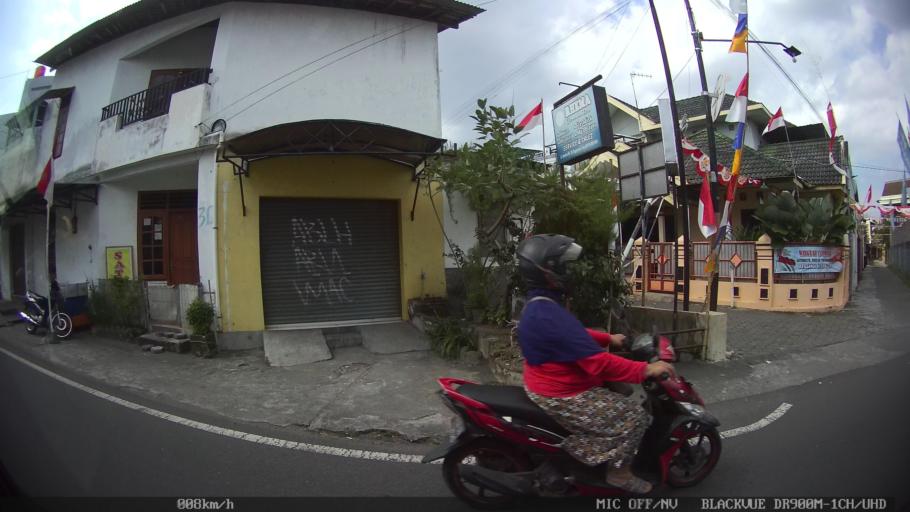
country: ID
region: Daerah Istimewa Yogyakarta
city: Yogyakarta
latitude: -7.7716
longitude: 110.3596
